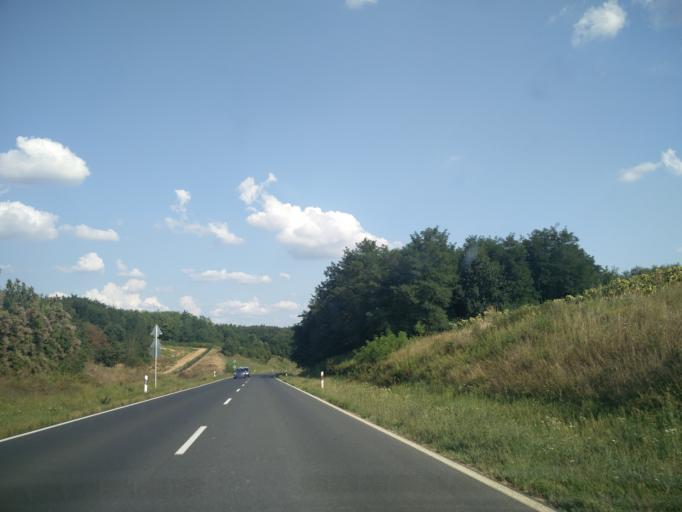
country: HU
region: Zala
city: Zalaegerszeg
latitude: 46.8797
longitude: 16.8437
